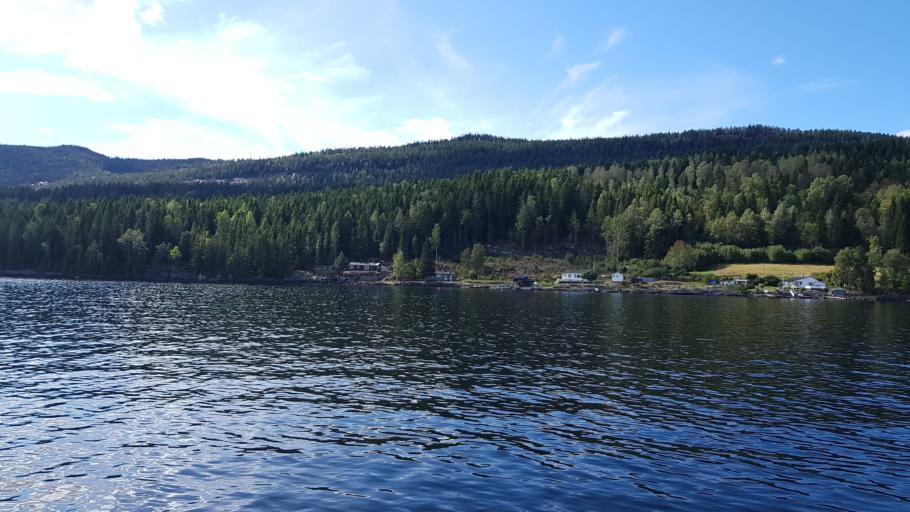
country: NO
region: Akershus
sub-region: Hurdal
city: Hurdal
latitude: 60.5436
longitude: 11.1987
